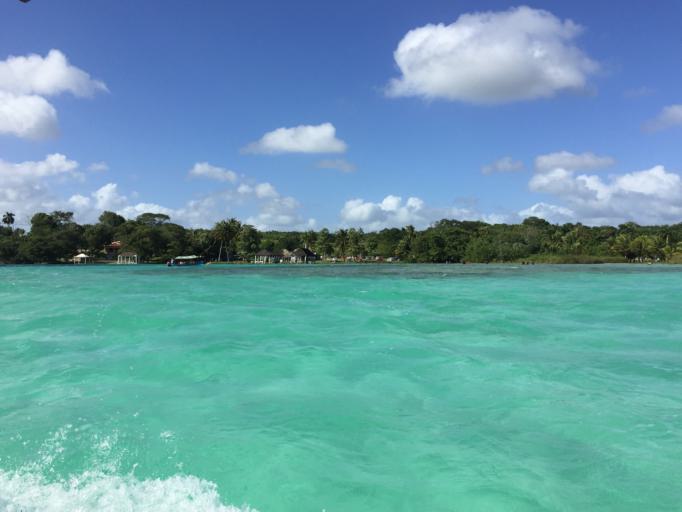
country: MX
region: Quintana Roo
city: Bacalar
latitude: 18.6501
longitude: -88.4077
